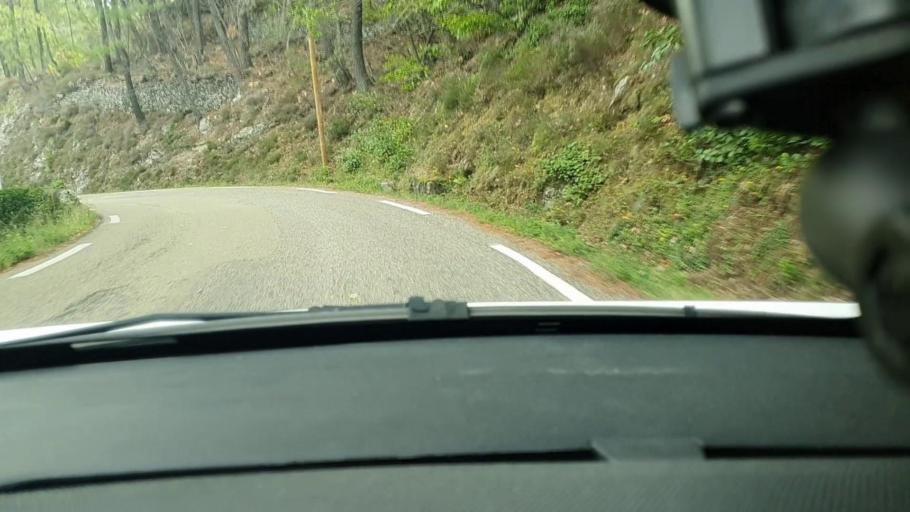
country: FR
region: Languedoc-Roussillon
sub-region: Departement du Gard
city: Besseges
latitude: 44.3060
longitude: 4.0563
